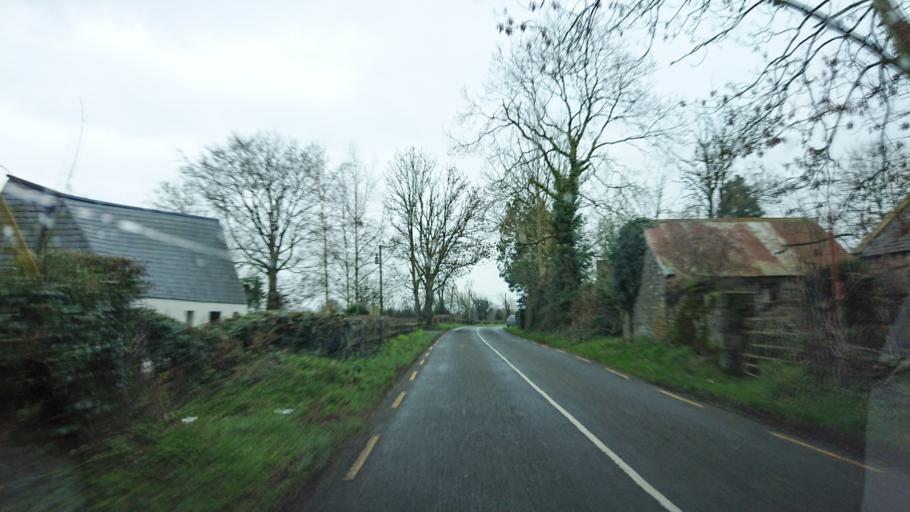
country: IE
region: Leinster
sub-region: Kilkenny
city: Callan
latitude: 52.5344
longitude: -7.2929
